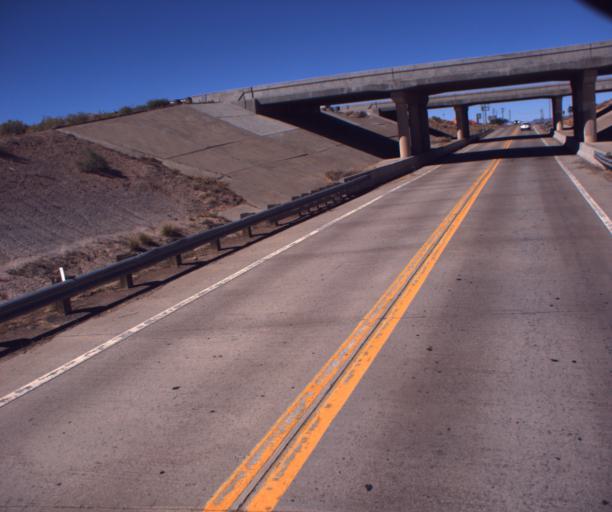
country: US
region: Arizona
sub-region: Navajo County
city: Holbrook
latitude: 34.9729
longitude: -110.0864
